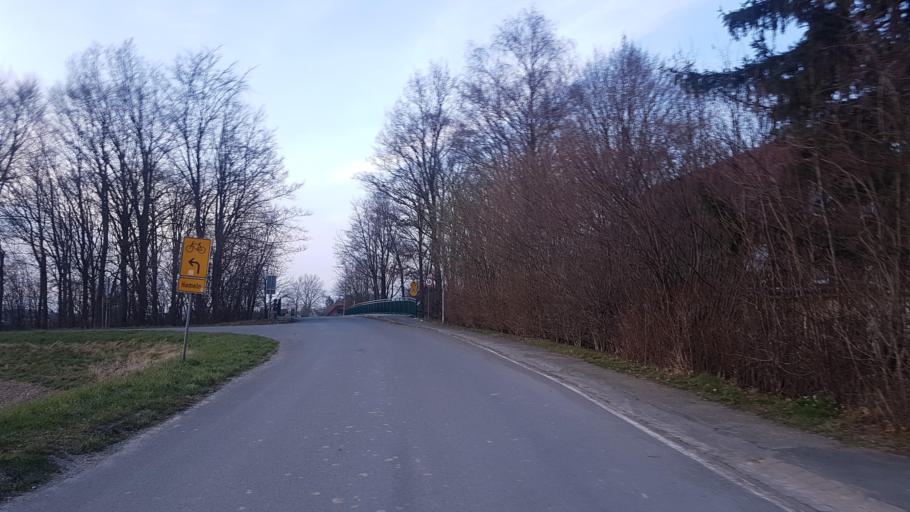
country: DE
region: Lower Saxony
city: Bad Munder am Deister
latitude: 52.1618
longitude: 9.4757
